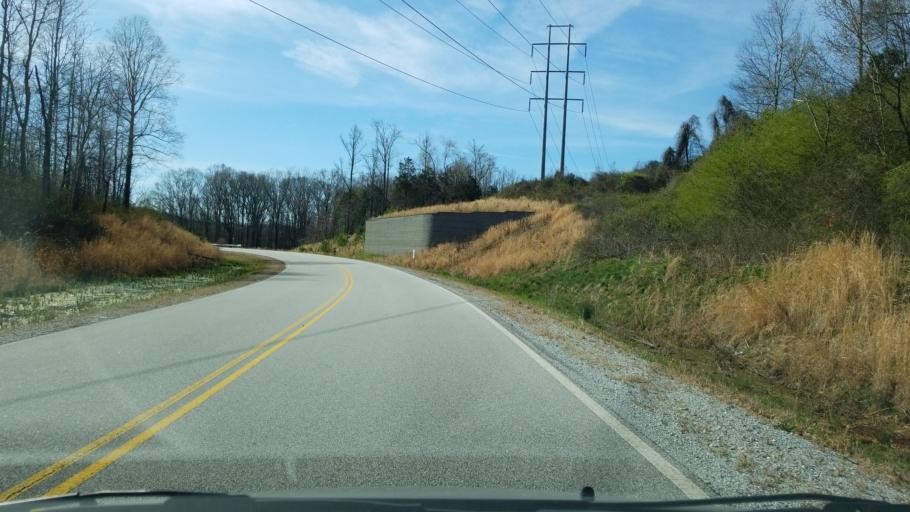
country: US
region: Tennessee
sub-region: Hamilton County
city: Harrison
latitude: 35.0970
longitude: -85.1368
